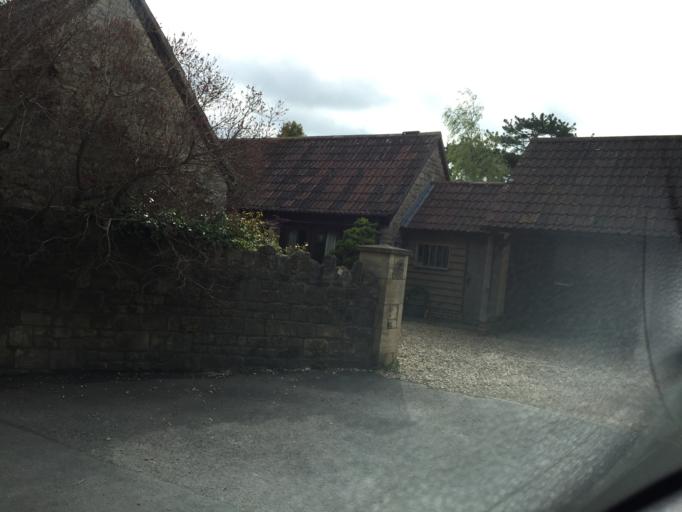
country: GB
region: England
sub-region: Bath and North East Somerset
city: Freshford
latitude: 51.3564
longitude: -2.3290
